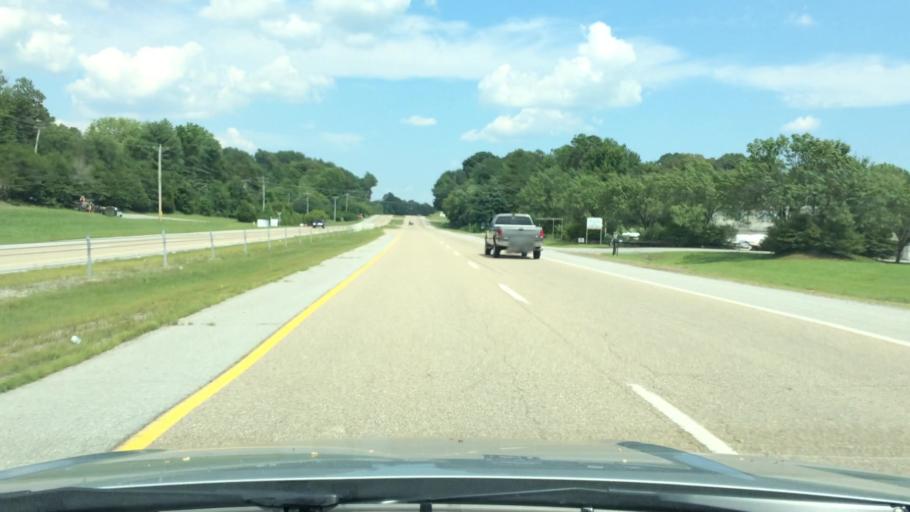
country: US
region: Tennessee
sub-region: Loudon County
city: Lenoir City
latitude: 35.8416
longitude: -84.3096
